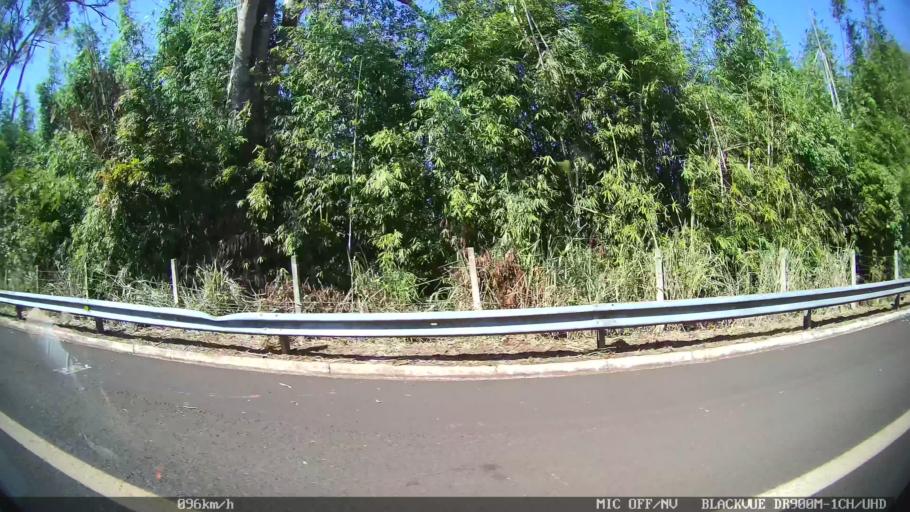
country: BR
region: Sao Paulo
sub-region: Batatais
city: Batatais
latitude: -20.7310
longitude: -47.5235
